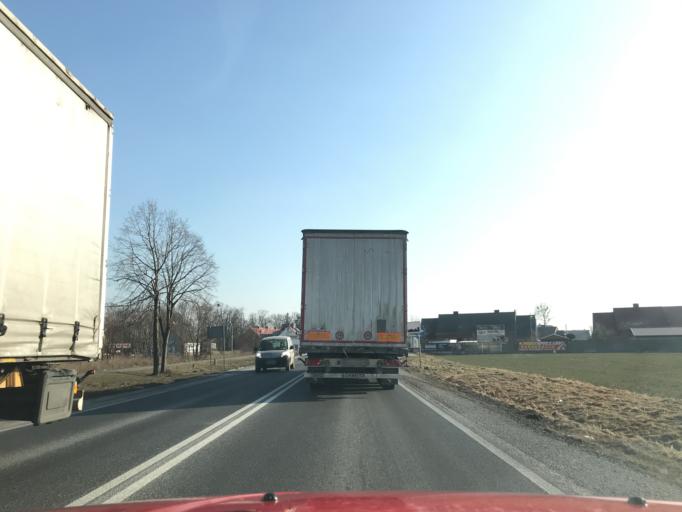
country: PL
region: Greater Poland Voivodeship
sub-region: Powiat sredzki
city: Nowe Miasto nad Warta
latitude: 52.0769
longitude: 17.4183
